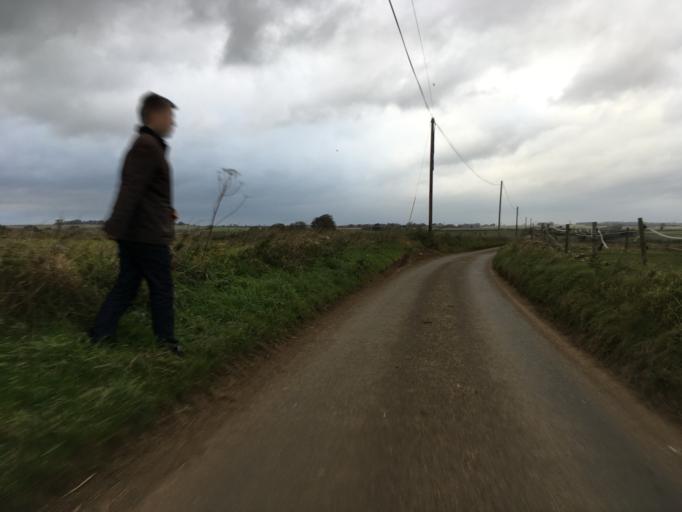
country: GB
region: England
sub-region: South Gloucestershire
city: Marshfield
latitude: 51.4660
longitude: -2.3238
